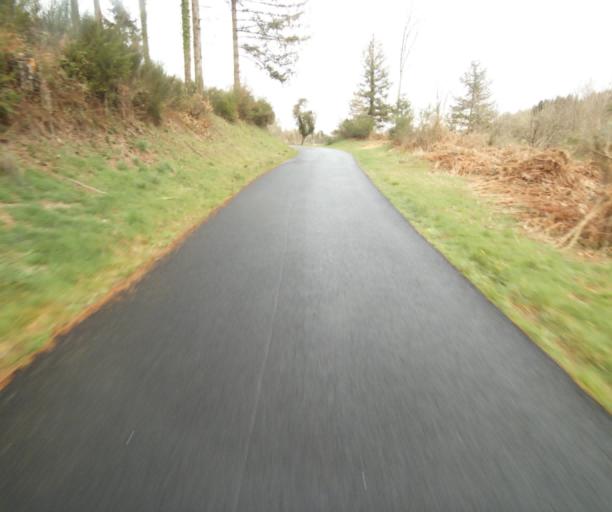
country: FR
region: Limousin
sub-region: Departement de la Correze
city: Saint-Privat
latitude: 45.2150
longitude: 2.0140
